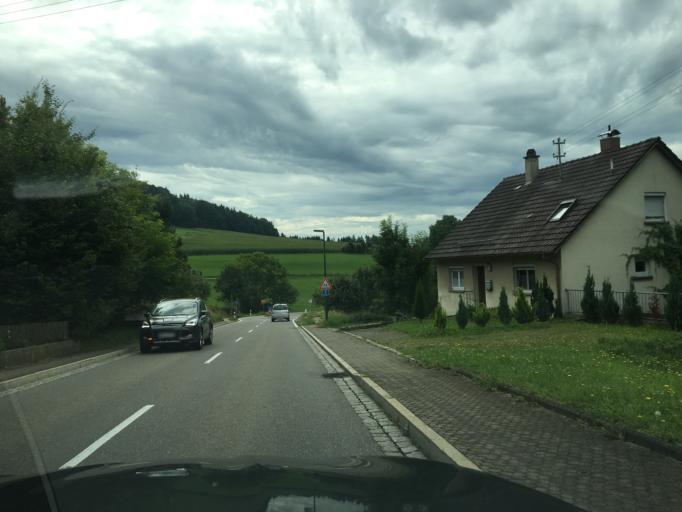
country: DE
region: Baden-Wuerttemberg
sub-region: Tuebingen Region
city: Rot
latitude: 47.8734
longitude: 9.1092
